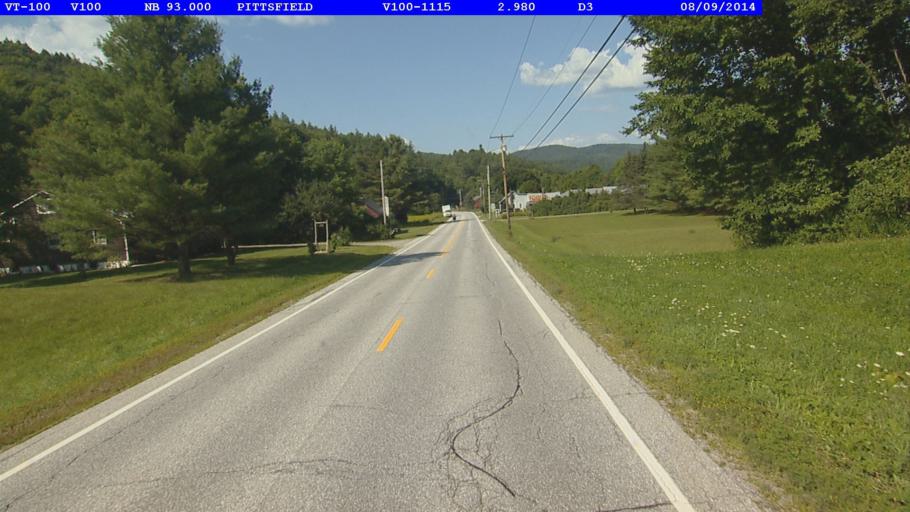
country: US
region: Vermont
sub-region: Rutland County
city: Rutland
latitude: 43.7597
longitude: -72.8192
